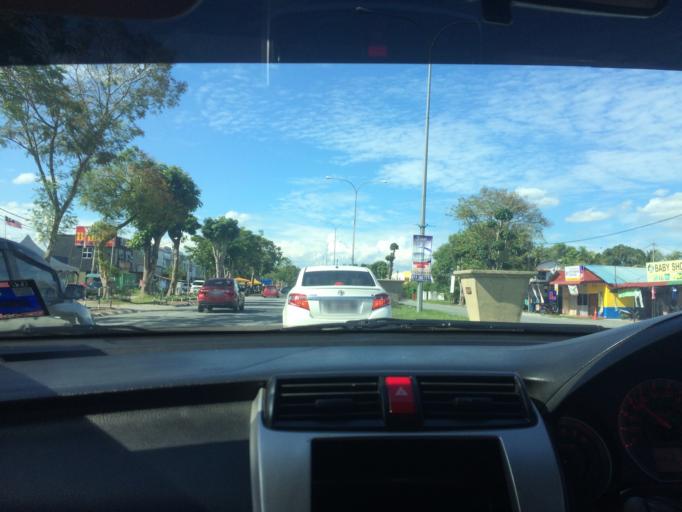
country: MY
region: Kedah
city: Jitra
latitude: 6.2053
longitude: 100.4134
